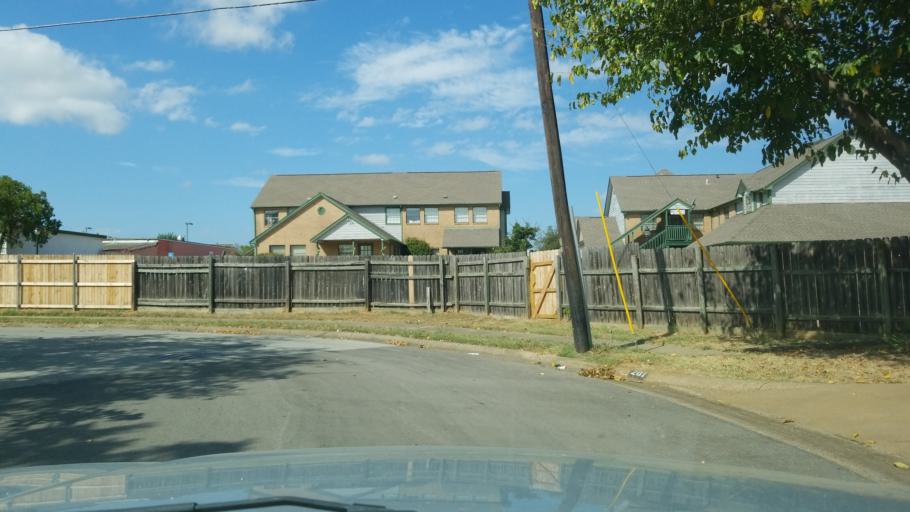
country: US
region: Texas
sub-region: Tarrant County
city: Euless
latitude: 32.8423
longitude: -97.0812
